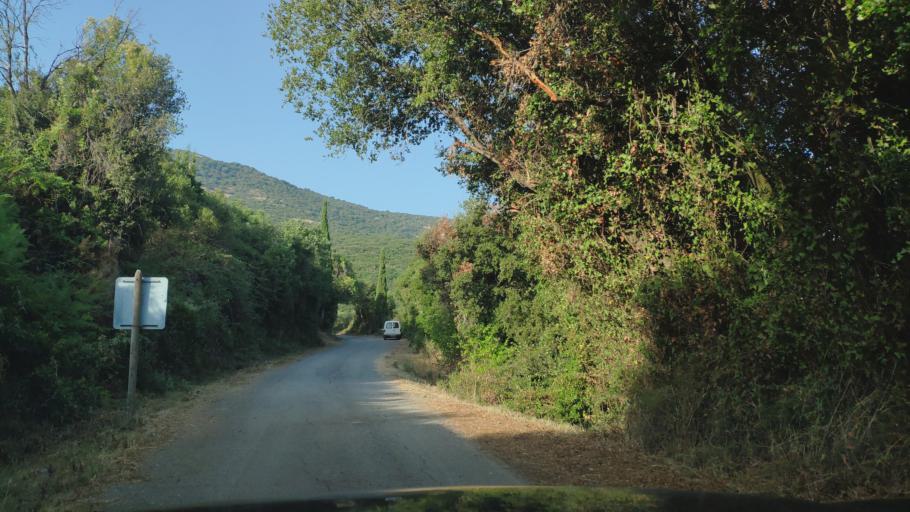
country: GR
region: West Greece
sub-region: Nomos Aitolias kai Akarnanias
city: Monastirakion
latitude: 38.8523
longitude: 20.9806
